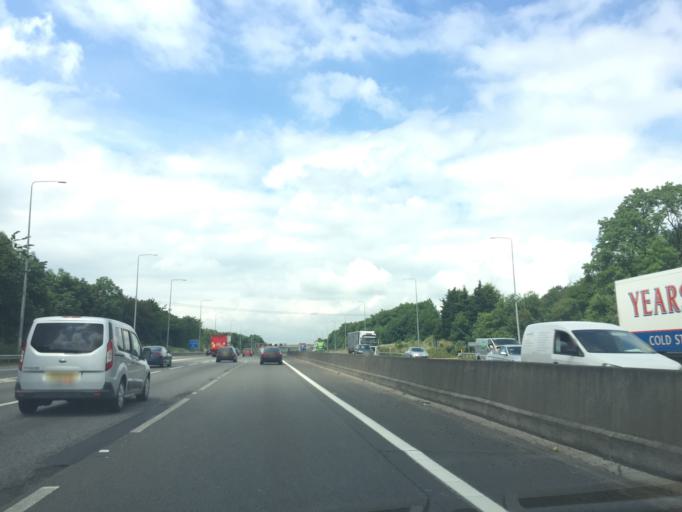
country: GB
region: England
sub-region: Buckinghamshire
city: Gerrards Cross
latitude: 51.5705
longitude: -0.5352
